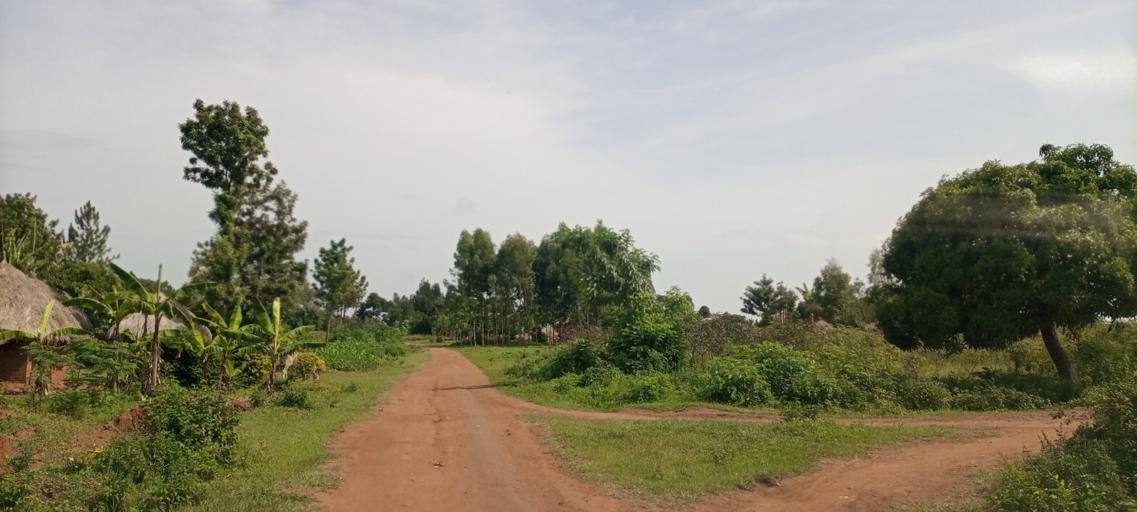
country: UG
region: Eastern Region
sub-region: Budaka District
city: Budaka
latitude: 1.1333
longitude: 34.0205
